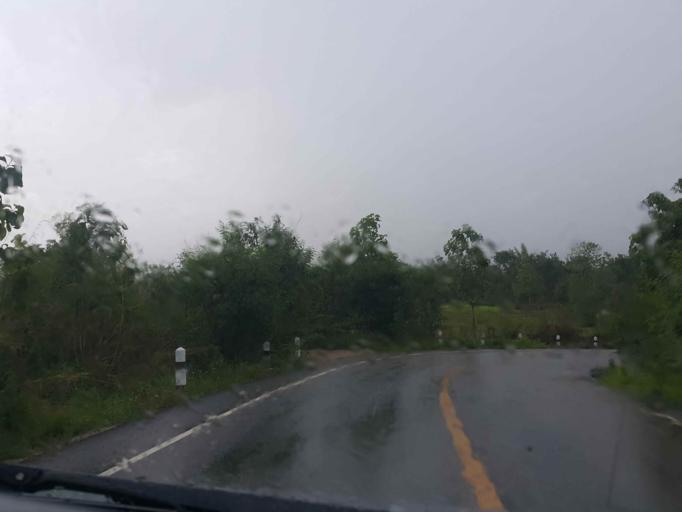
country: TH
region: Phayao
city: Dok Kham Tai
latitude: 19.0288
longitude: 99.9687
